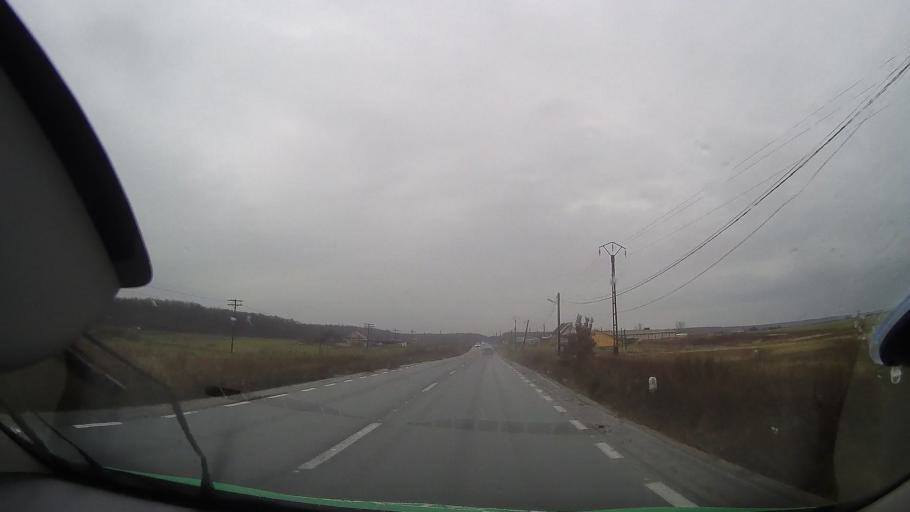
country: RO
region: Bihor
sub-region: Comuna Olcea
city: Olcea
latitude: 46.6866
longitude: 21.9660
